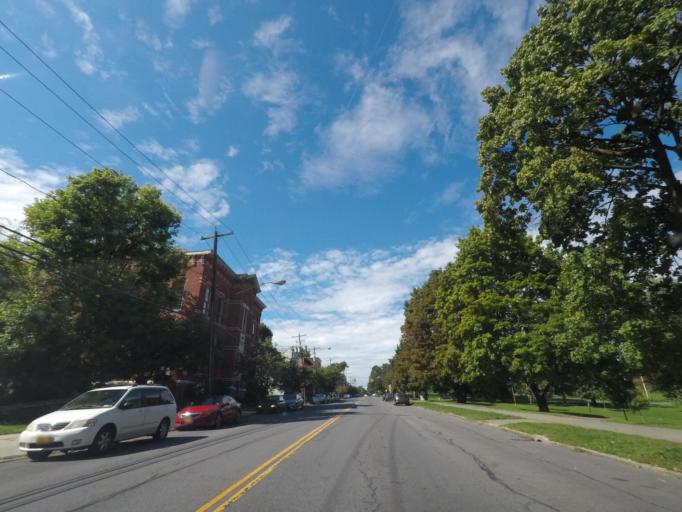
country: US
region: New York
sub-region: Albany County
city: Albany
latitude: 42.6442
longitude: -73.7664
